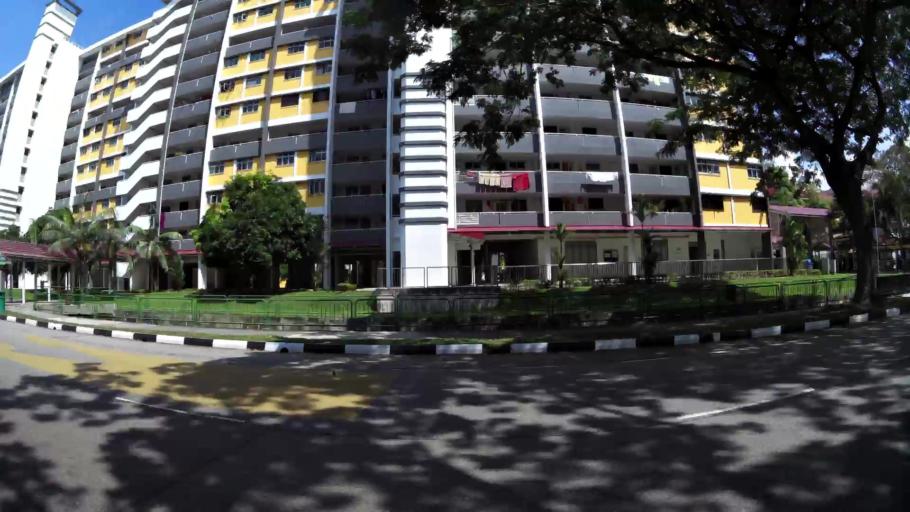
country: SG
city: Singapore
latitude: 1.3772
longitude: 103.8409
